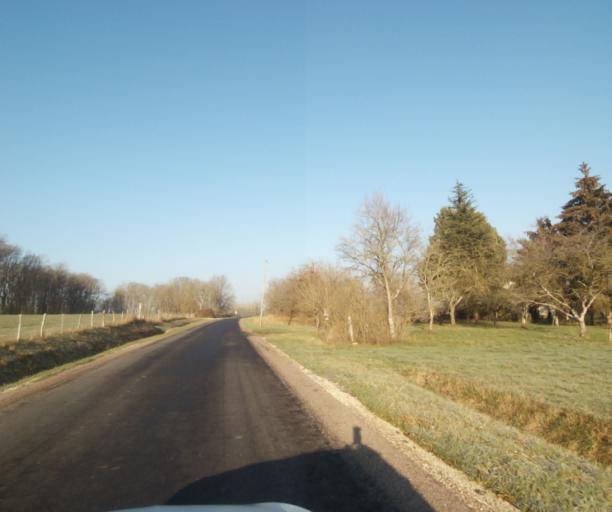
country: FR
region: Champagne-Ardenne
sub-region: Departement de la Haute-Marne
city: Montier-en-Der
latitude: 48.4870
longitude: 4.7393
